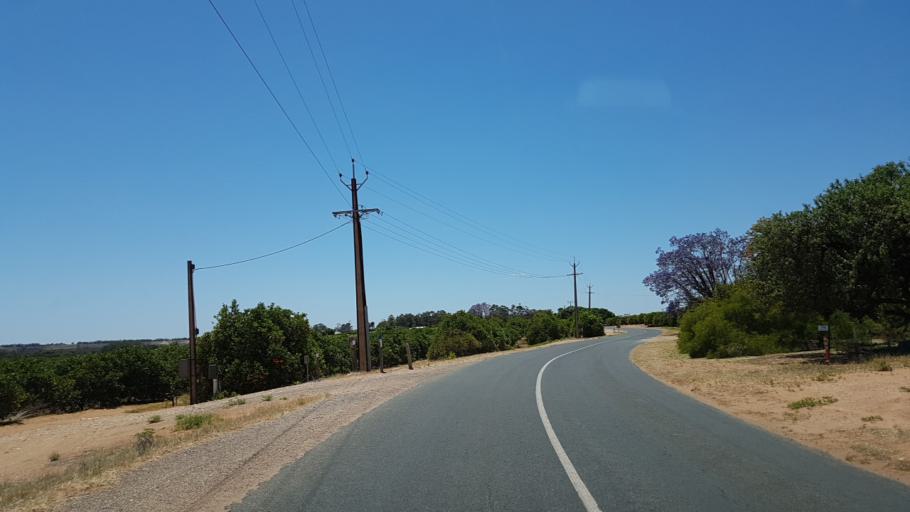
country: AU
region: South Australia
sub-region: Loxton Waikerie
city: Waikerie
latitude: -34.1762
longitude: 140.0275
